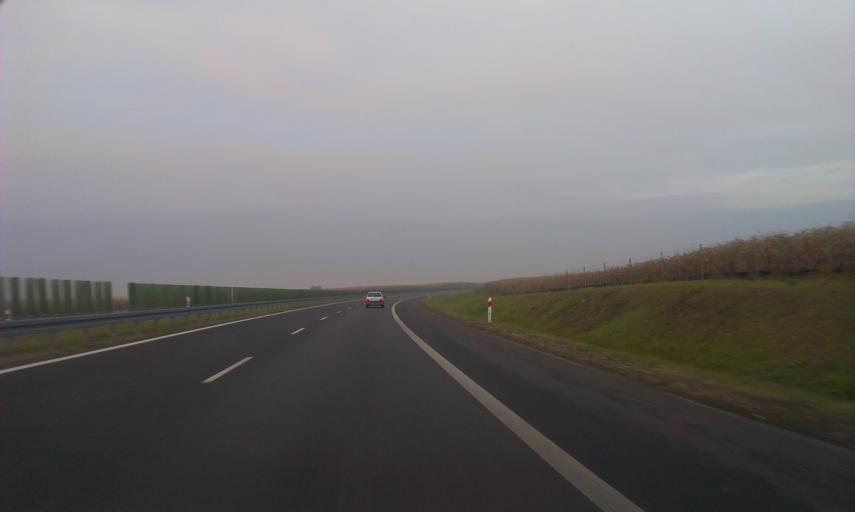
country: PL
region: Greater Poland Voivodeship
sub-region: Powiat poznanski
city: Zlotniki
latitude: 52.5130
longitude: 16.8146
